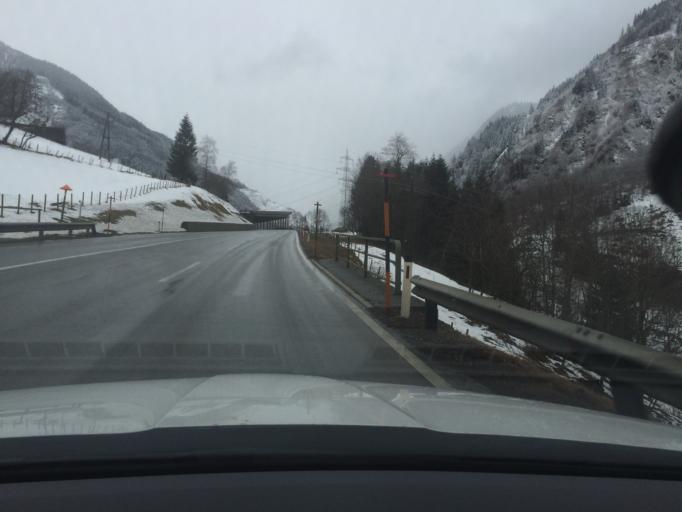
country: AT
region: Salzburg
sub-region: Politischer Bezirk Zell am See
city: Mittersill
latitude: 47.2336
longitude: 12.4940
